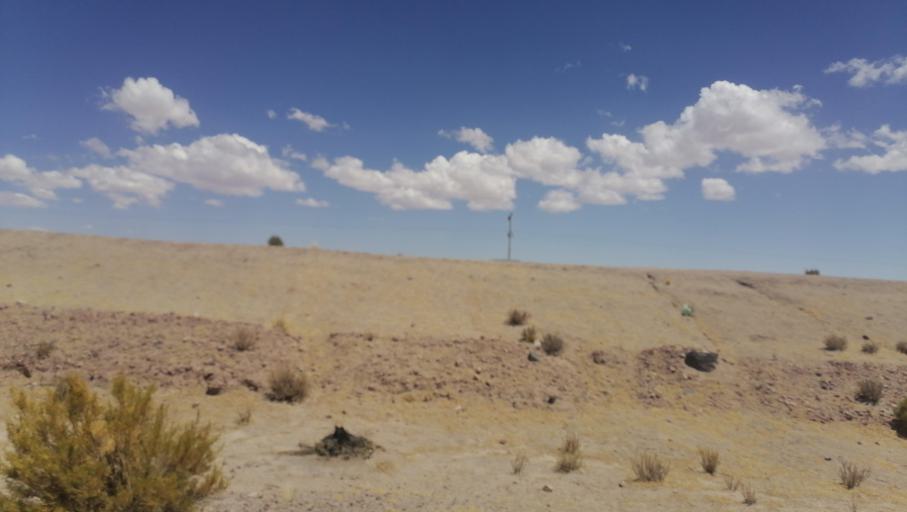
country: BO
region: Oruro
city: Challapata
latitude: -19.2190
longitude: -66.9988
